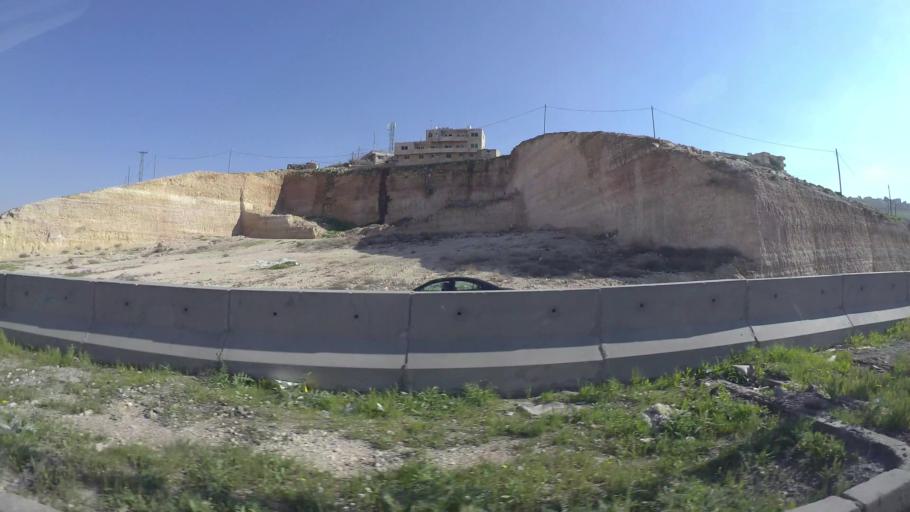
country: JO
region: Zarqa
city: Russeifa
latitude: 32.0258
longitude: 35.9774
